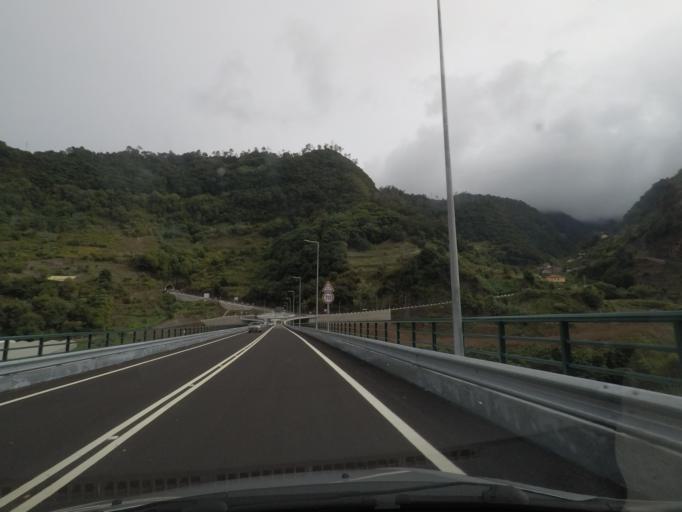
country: PT
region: Madeira
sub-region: Santana
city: Santana
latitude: 32.8168
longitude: -16.9025
